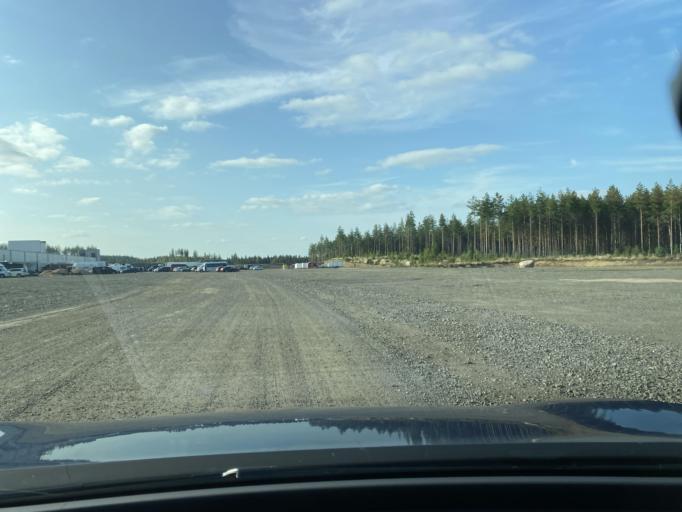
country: FI
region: Kymenlaakso
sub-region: Kouvola
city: Iitti
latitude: 60.8817
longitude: 26.4892
